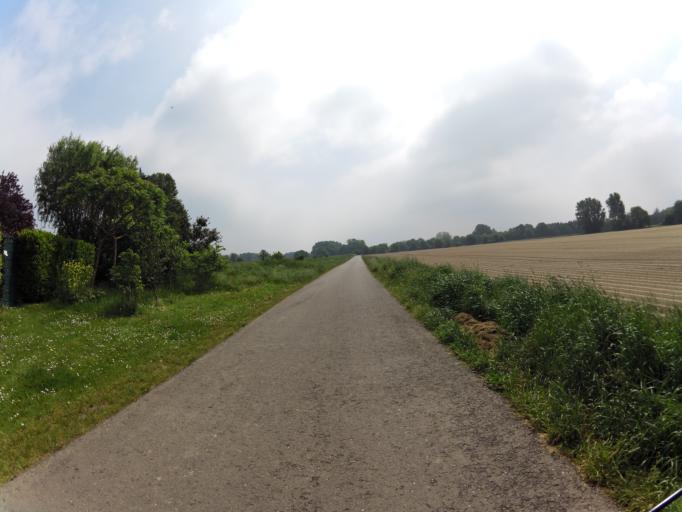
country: DE
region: North Rhine-Westphalia
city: Huckelhoven
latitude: 51.0574
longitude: 6.1921
